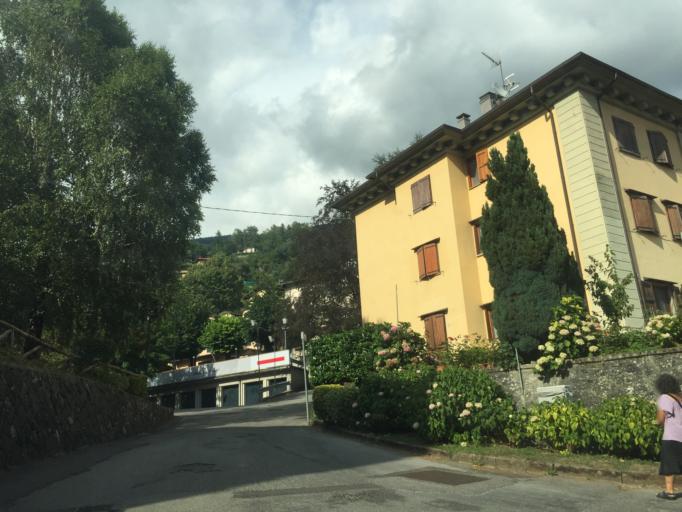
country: IT
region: Tuscany
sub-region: Provincia di Pistoia
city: Cutigliano
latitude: 44.0992
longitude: 10.7534
